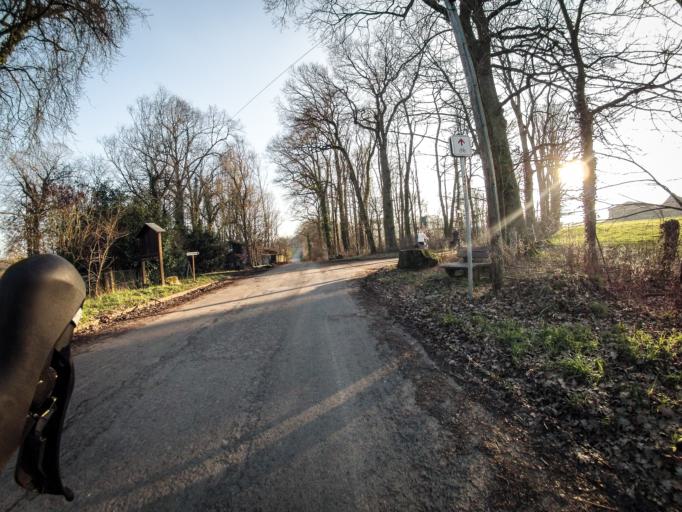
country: DE
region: North Rhine-Westphalia
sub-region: Regierungsbezirk Munster
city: Tecklenburg
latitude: 52.2560
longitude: 7.8340
